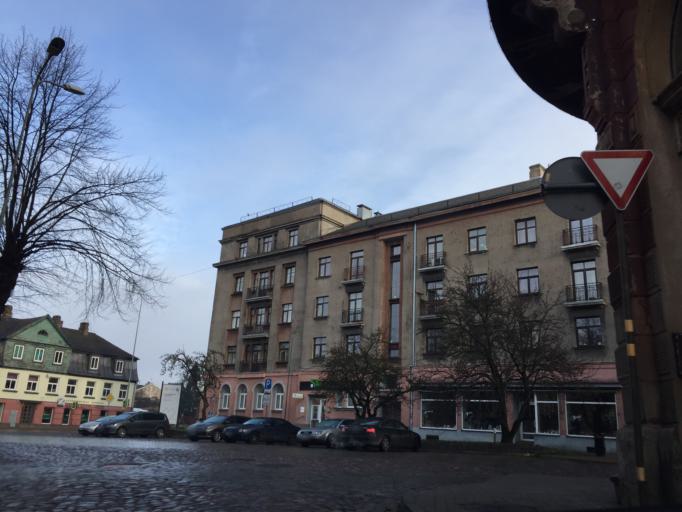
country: LV
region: Liepaja
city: Liepaja
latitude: 56.5091
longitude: 21.0074
